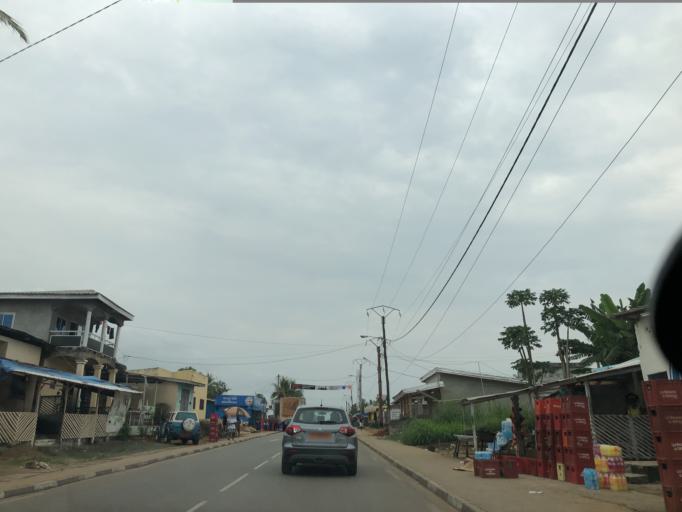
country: CM
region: South Province
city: Kribi
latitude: 2.9362
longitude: 9.9057
